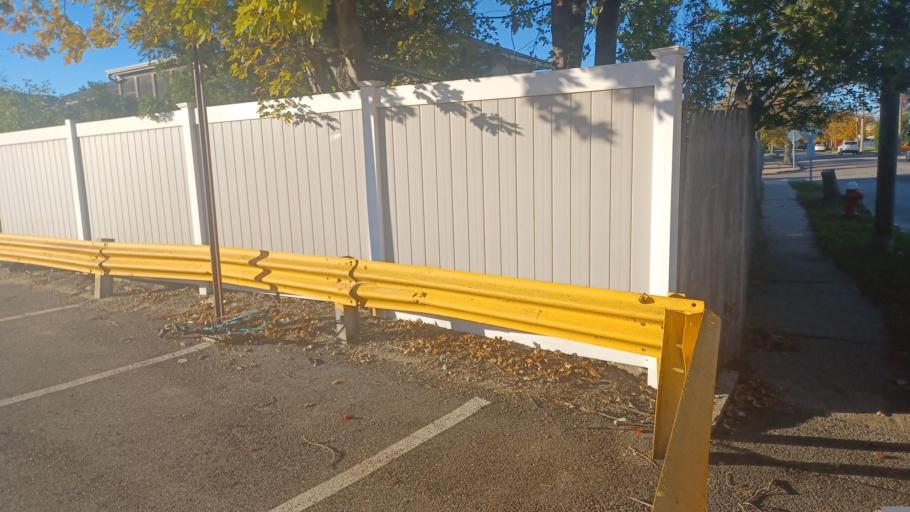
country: US
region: New York
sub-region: Nassau County
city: Oceanside
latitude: 40.6235
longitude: -73.6420
